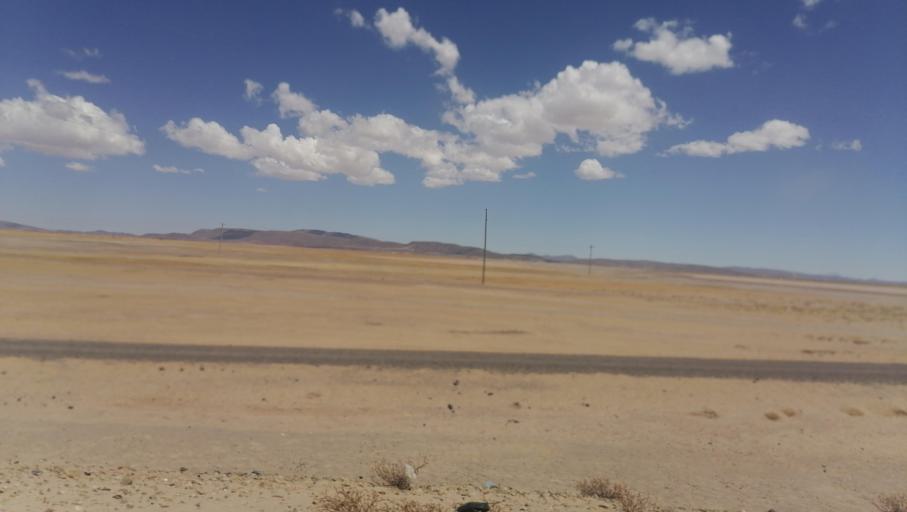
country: BO
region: Oruro
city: Challapata
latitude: -19.2136
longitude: -67.0228
